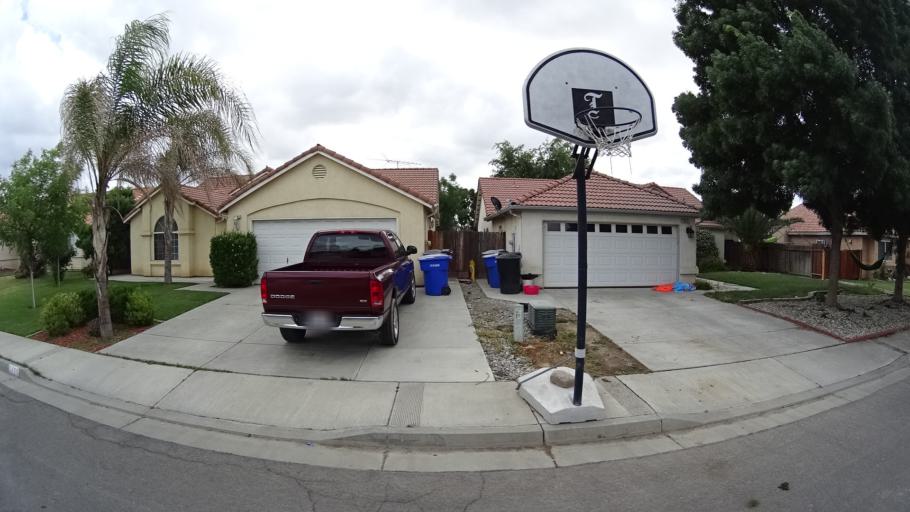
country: US
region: California
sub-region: Kings County
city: Home Garden
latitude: 36.3067
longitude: -119.6612
